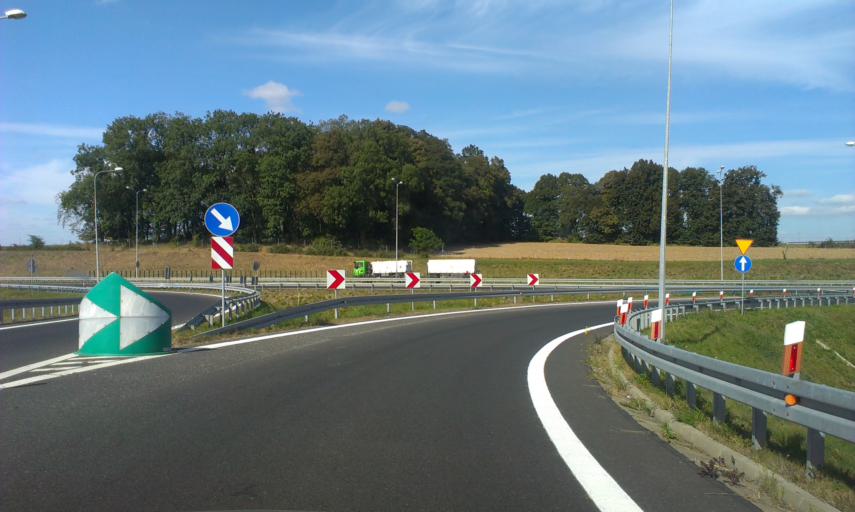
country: PL
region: Greater Poland Voivodeship
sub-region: Powiat pilski
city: Wyrzysk
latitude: 53.1621
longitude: 17.2223
